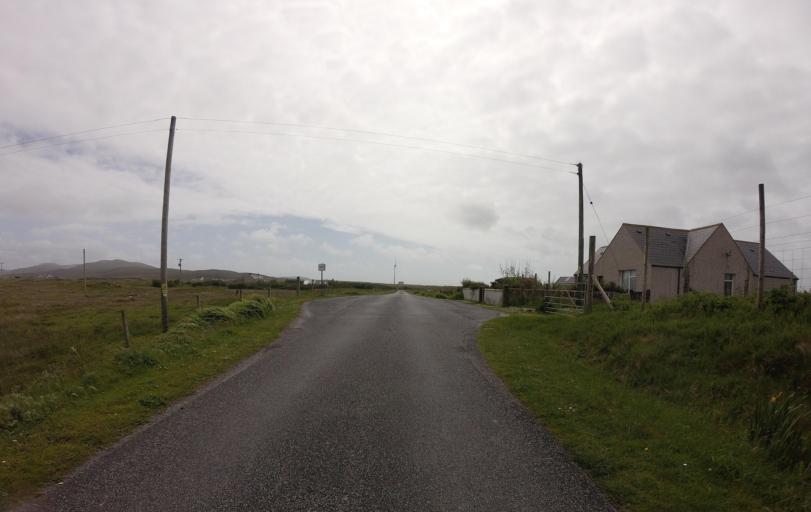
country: GB
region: Scotland
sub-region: Eilean Siar
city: Isle of South Uist
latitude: 57.2474
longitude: -7.4045
